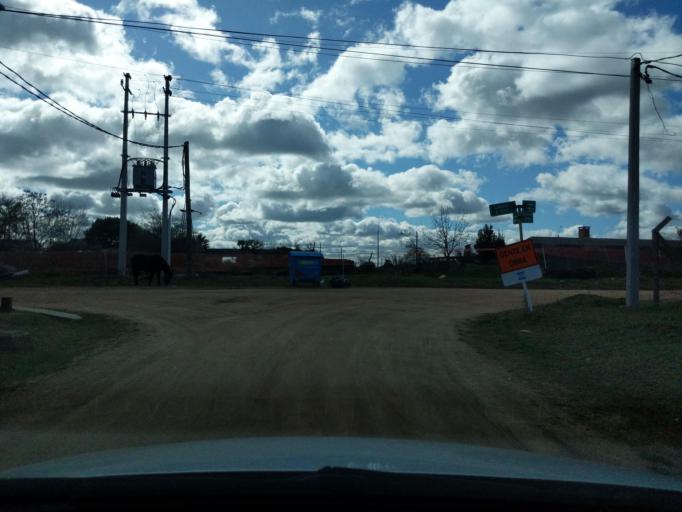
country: UY
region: Florida
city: Florida
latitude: -34.0793
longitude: -56.2248
